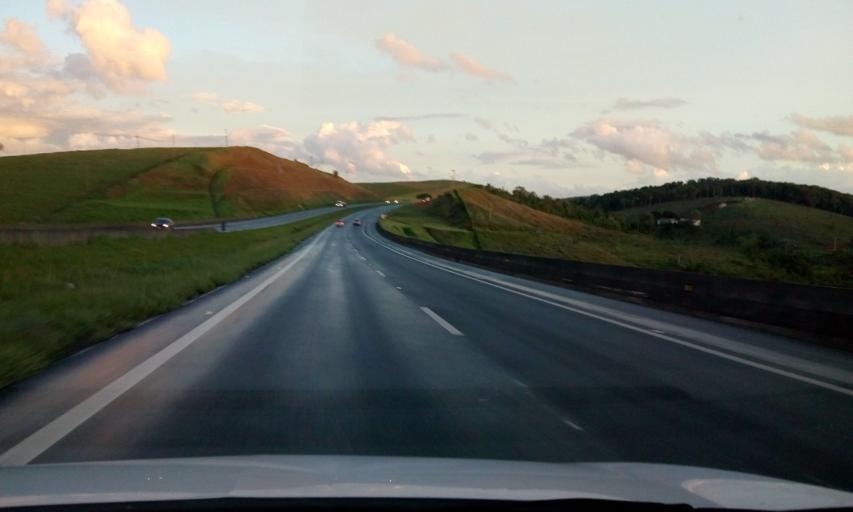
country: BR
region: Sao Paulo
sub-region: Santa Isabel
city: Santa Isabel
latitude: -23.2470
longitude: -46.1116
